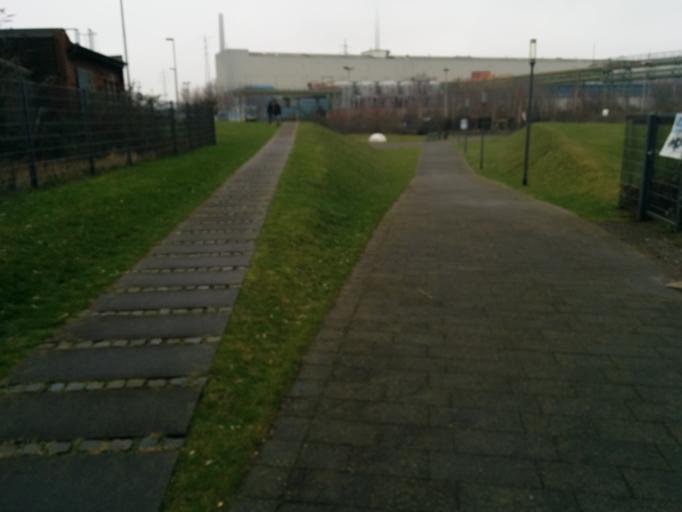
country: DE
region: North Rhine-Westphalia
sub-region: Regierungsbezirk Dusseldorf
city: Hochfeld
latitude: 51.4133
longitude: 6.7440
